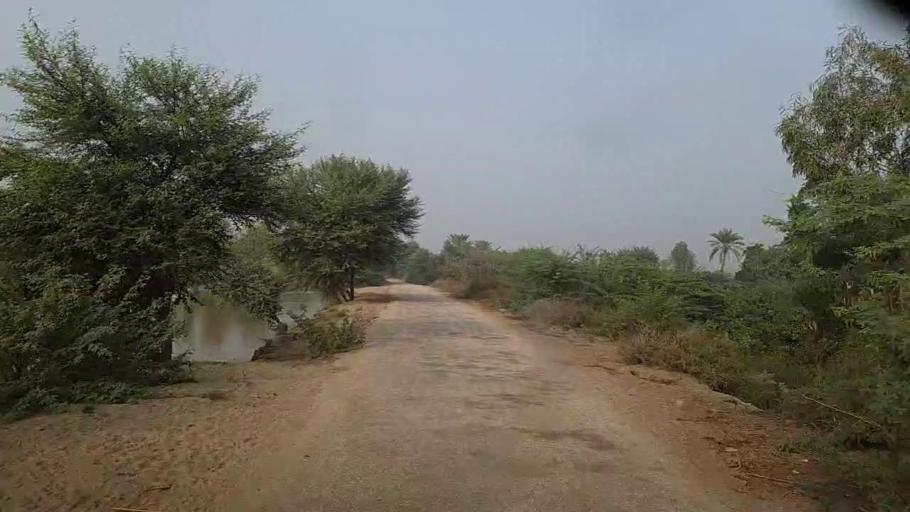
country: PK
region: Sindh
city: Bozdar
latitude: 27.1565
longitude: 68.6605
